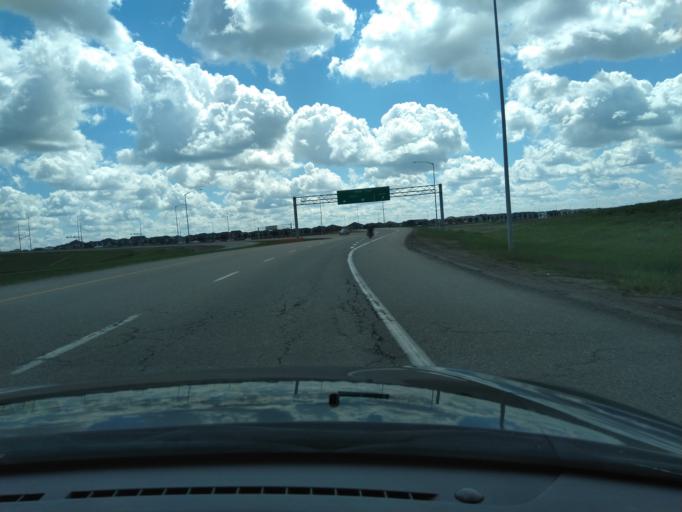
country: CA
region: Alberta
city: Airdrie
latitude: 51.1745
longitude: -113.9733
